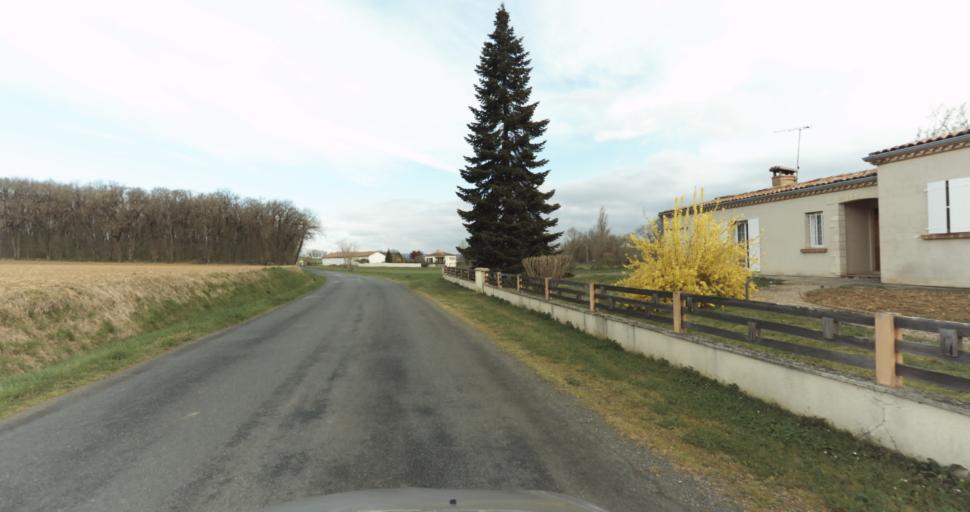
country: FR
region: Midi-Pyrenees
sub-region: Departement du Tarn
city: Puygouzon
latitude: 43.9041
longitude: 2.1842
